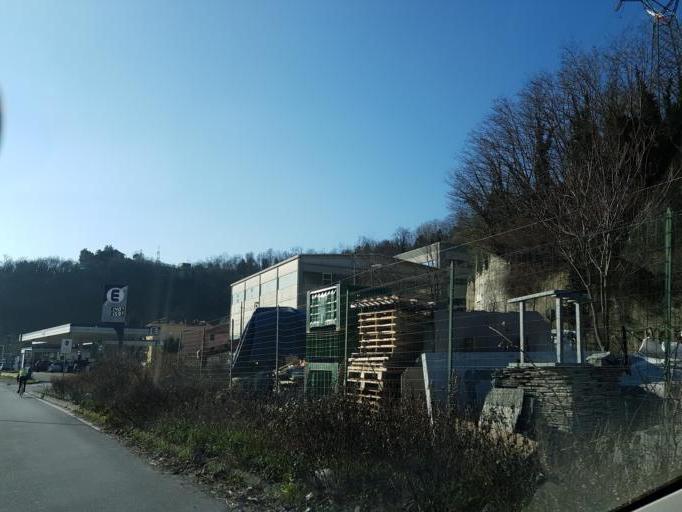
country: IT
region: Liguria
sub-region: Provincia di Genova
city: Santa Marta
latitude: 44.4872
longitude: 8.8983
